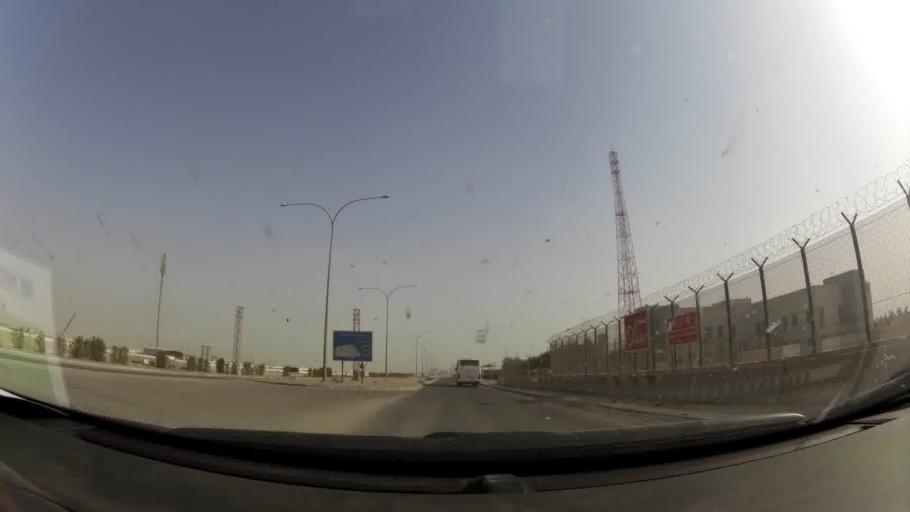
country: KW
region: Al Ahmadi
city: Al Ahmadi
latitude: 28.9935
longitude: 48.1070
